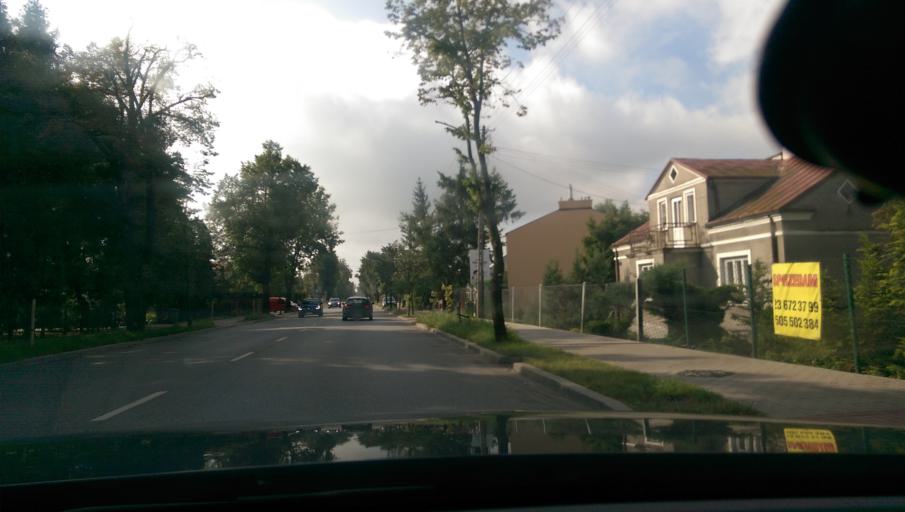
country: PL
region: Masovian Voivodeship
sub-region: Powiat ciechanowski
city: Ciechanow
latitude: 52.8671
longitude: 20.6255
